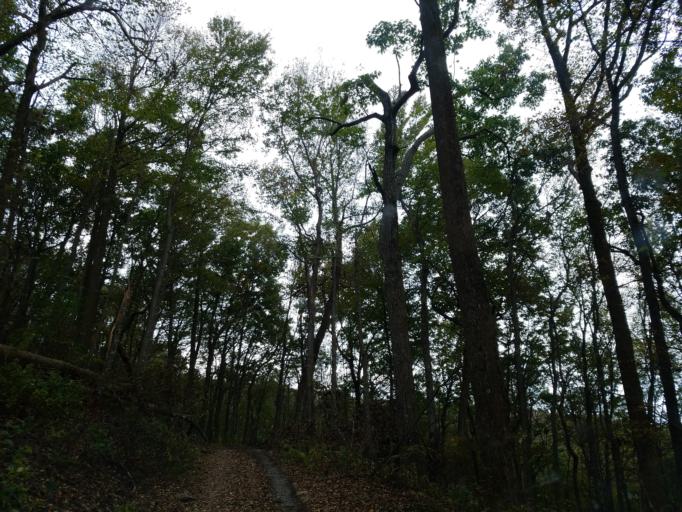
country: US
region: Georgia
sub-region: Dawson County
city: Dawsonville
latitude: 34.6079
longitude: -84.2153
